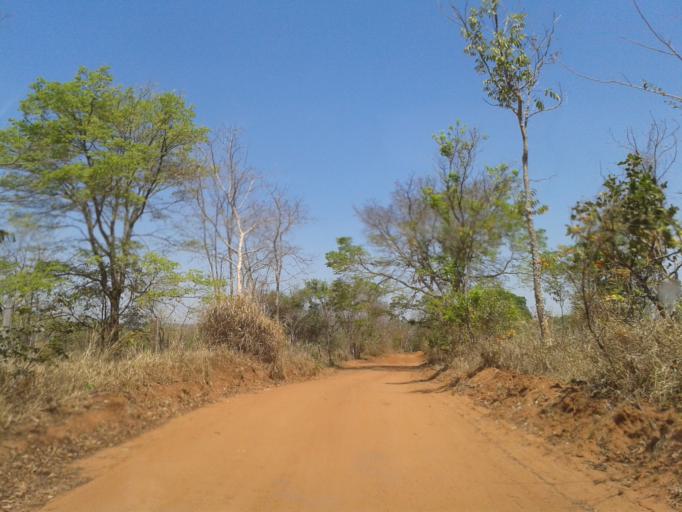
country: BR
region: Minas Gerais
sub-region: Ituiutaba
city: Ituiutaba
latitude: -19.0950
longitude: -49.2973
